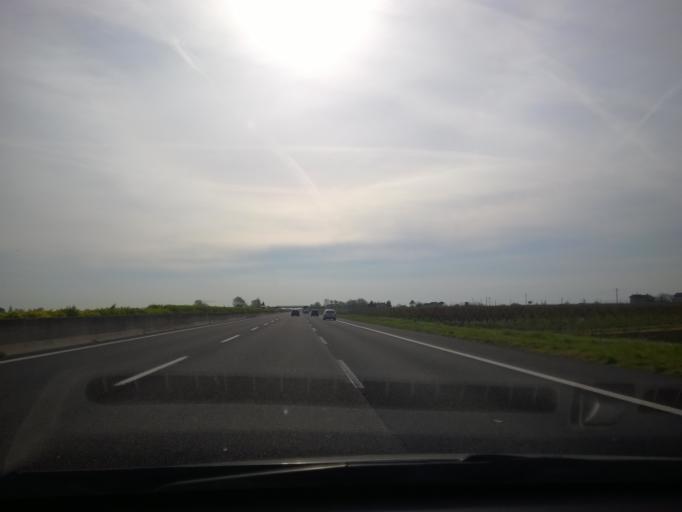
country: IT
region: Emilia-Romagna
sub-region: Forli-Cesena
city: Bagnarola
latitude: 44.1428
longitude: 12.3388
